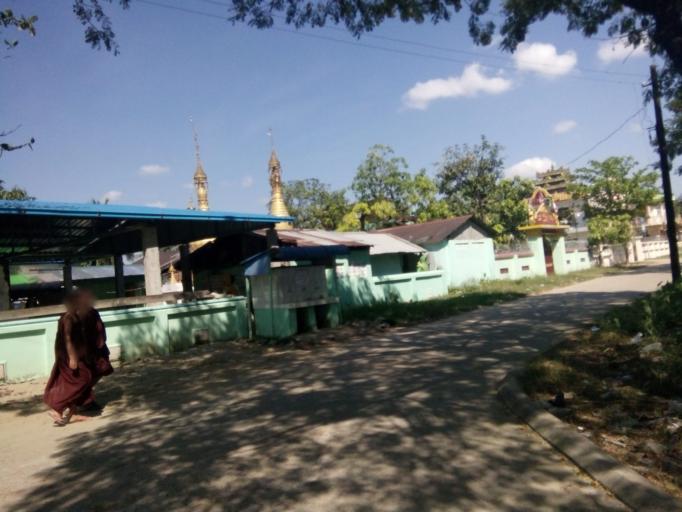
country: MM
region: Yangon
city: Yangon
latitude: 16.9197
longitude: 96.1578
